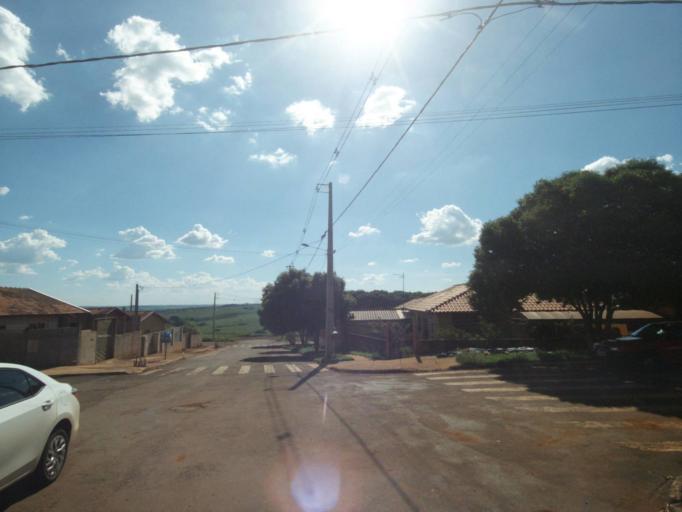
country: BR
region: Parana
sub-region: Sertanopolis
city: Sertanopolis
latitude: -23.0470
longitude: -50.8187
